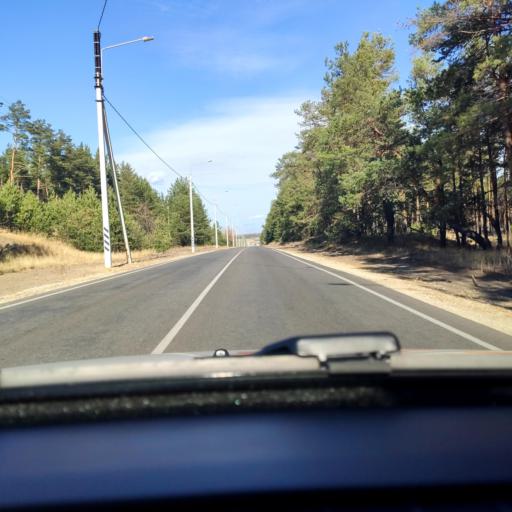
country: RU
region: Voronezj
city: Shilovo
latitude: 51.5300
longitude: 39.1410
